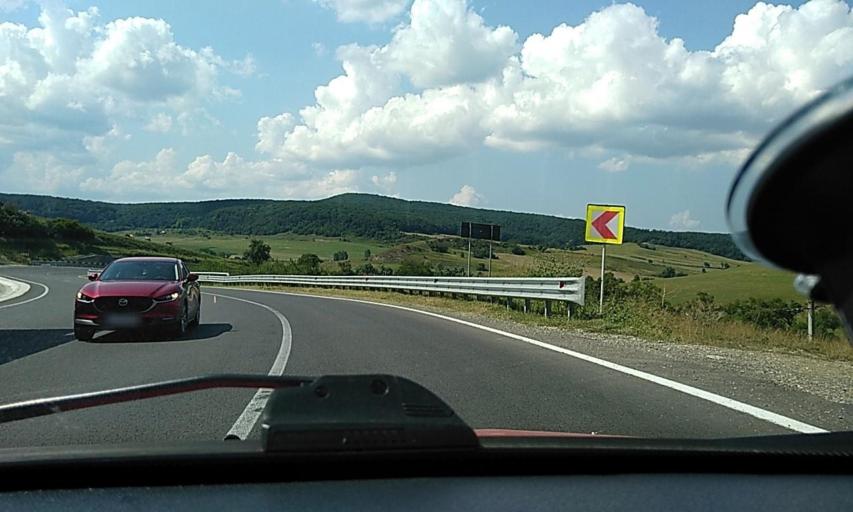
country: RO
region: Brasov
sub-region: Oras Rupea
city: Fiser
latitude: 46.0959
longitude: 25.1035
